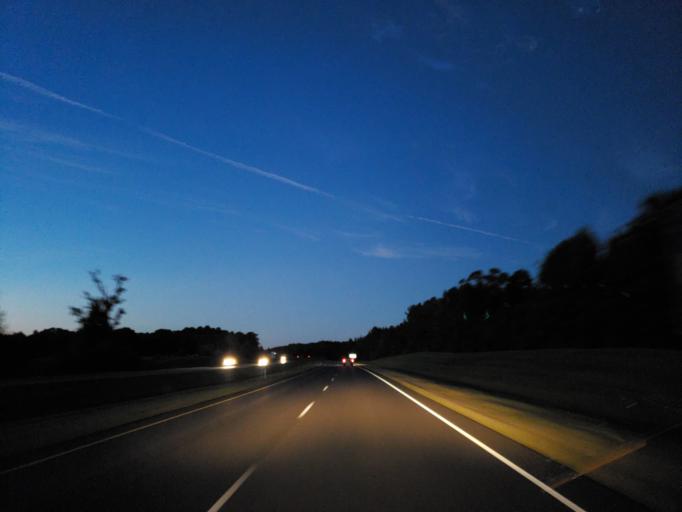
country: US
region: Mississippi
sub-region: Clarke County
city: Quitman
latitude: 32.0435
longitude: -88.6777
